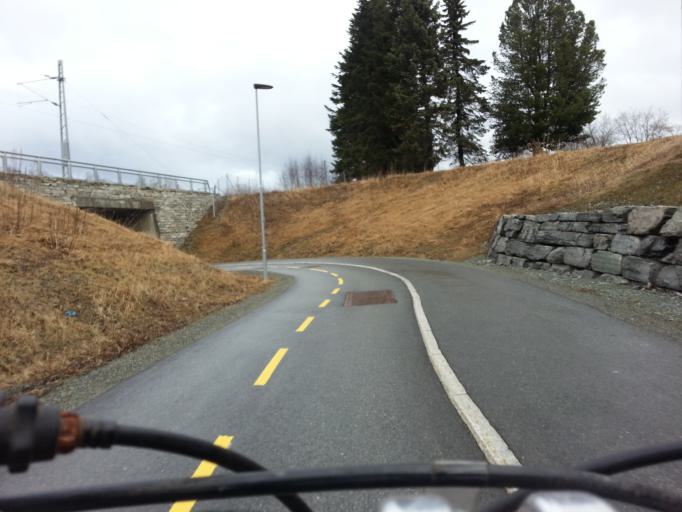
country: NO
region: Sor-Trondelag
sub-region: Trondheim
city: Trondheim
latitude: 63.4119
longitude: 10.3842
